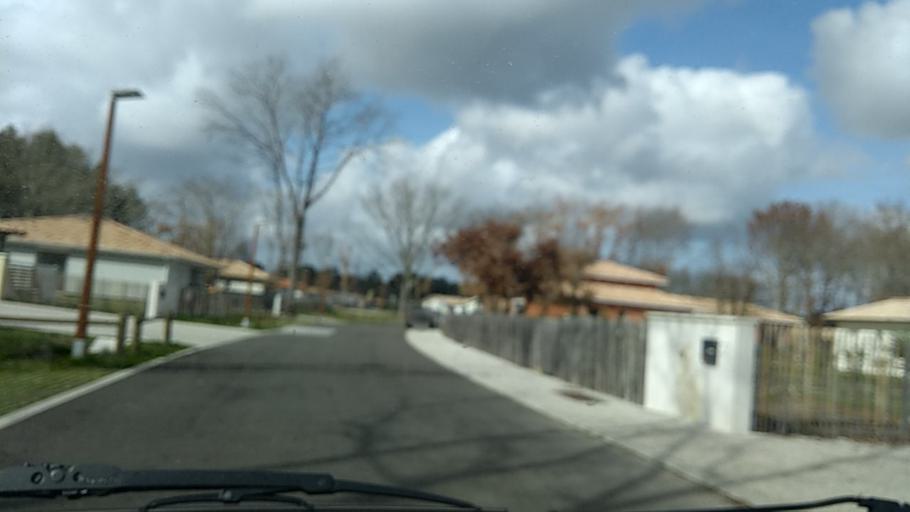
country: FR
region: Aquitaine
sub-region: Departement de la Gironde
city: Salles
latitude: 44.5455
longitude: -0.8753
